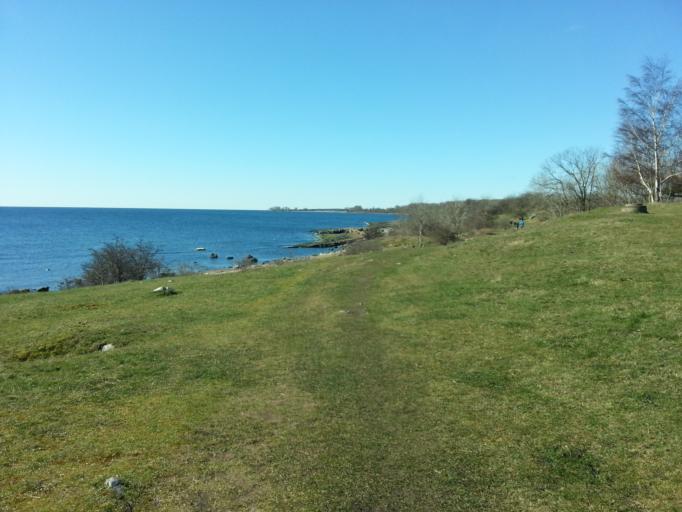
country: SE
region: Skane
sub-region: Simrishamns Kommun
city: Simrishamn
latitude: 55.5081
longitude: 14.3433
